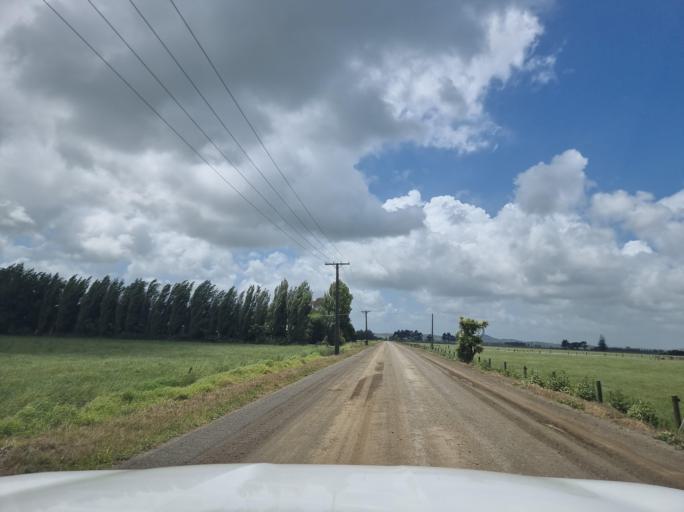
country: NZ
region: Northland
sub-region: Kaipara District
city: Dargaville
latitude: -36.0865
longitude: 174.0037
